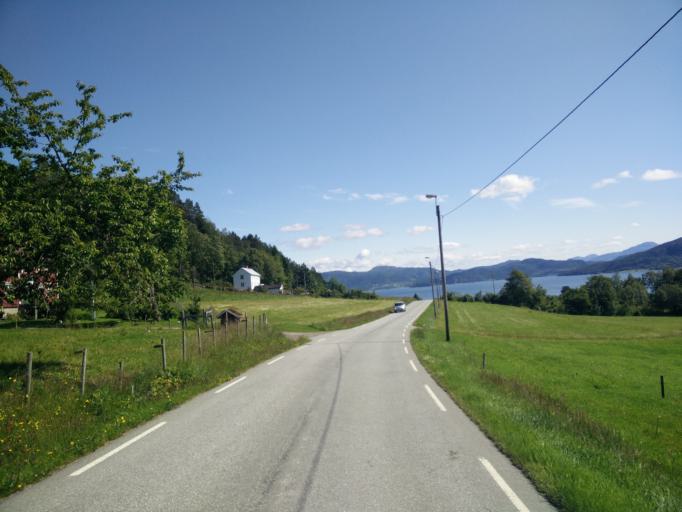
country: NO
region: More og Romsdal
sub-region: Kristiansund
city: Rensvik
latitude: 63.0385
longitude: 7.8316
